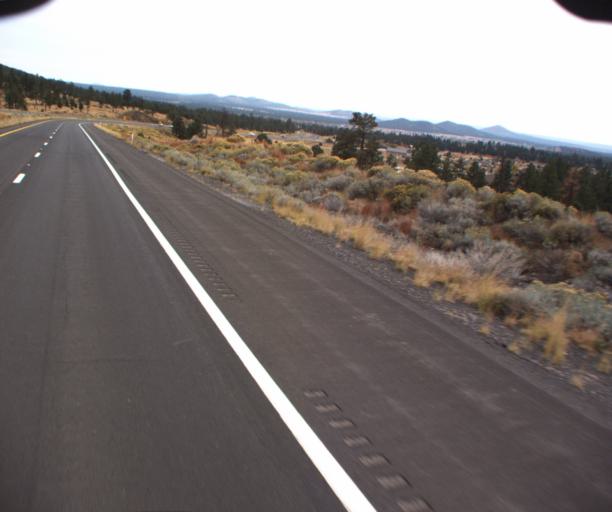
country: US
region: Arizona
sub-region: Coconino County
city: Flagstaff
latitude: 35.3500
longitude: -111.5667
